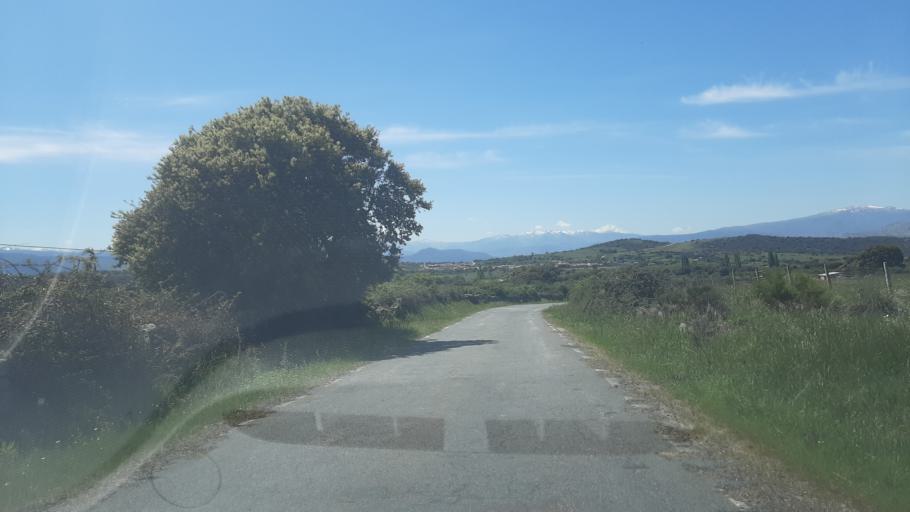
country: ES
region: Castille and Leon
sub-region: Provincia de Avila
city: Narrillos del Alamo
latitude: 40.5532
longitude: -5.4418
